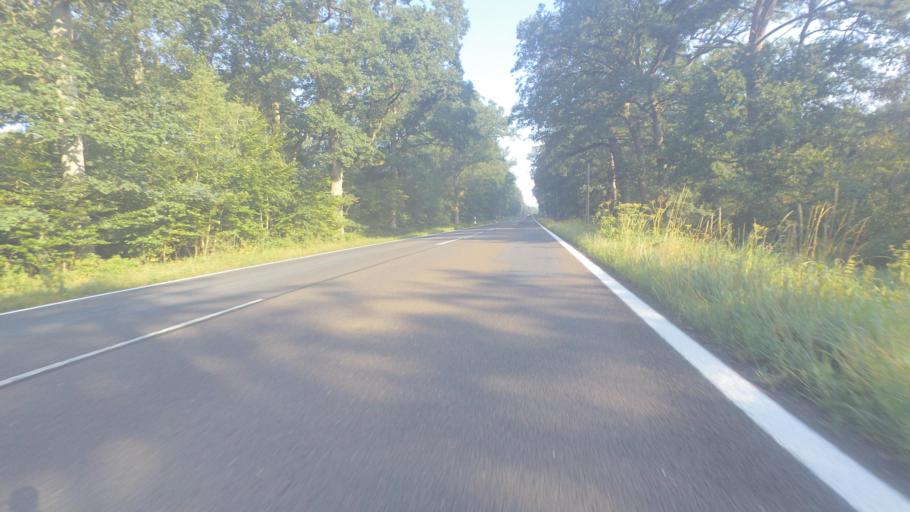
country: DE
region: Mecklenburg-Vorpommern
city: Grimmen
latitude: 54.0366
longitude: 13.1273
